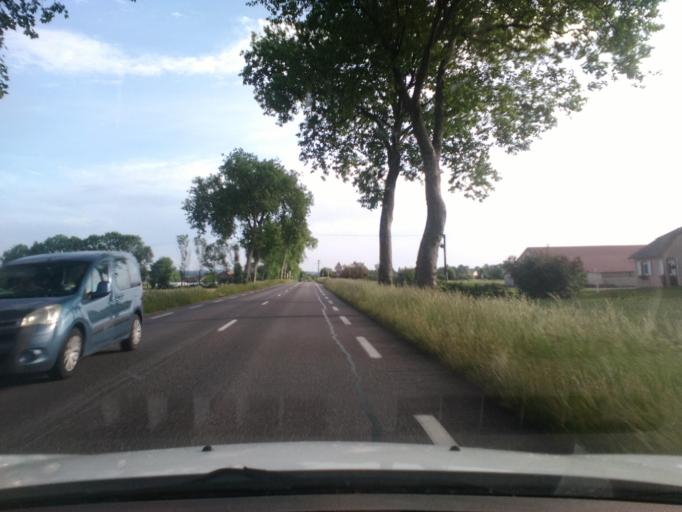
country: FR
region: Lorraine
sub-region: Departement de Meurthe-et-Moselle
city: Luneville
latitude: 48.5541
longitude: 6.4646
